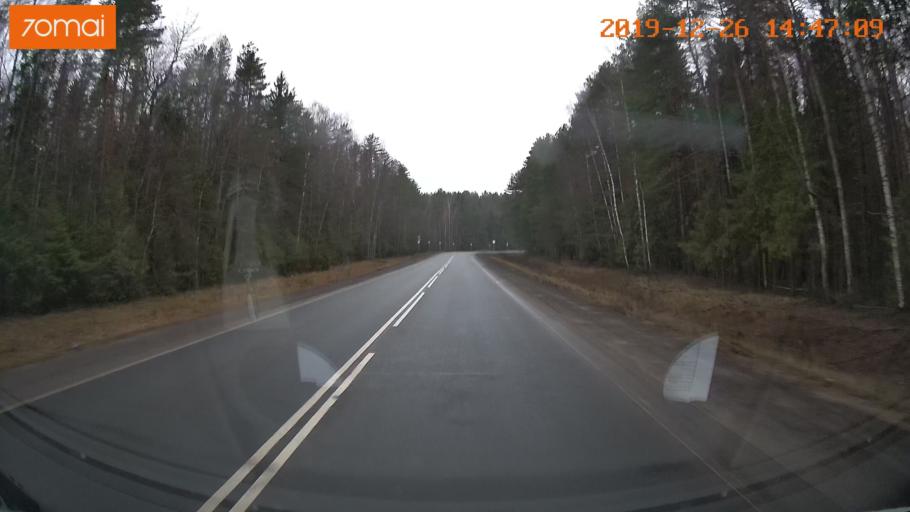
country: RU
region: Jaroslavl
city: Poshekhon'ye
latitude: 58.3411
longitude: 39.0048
